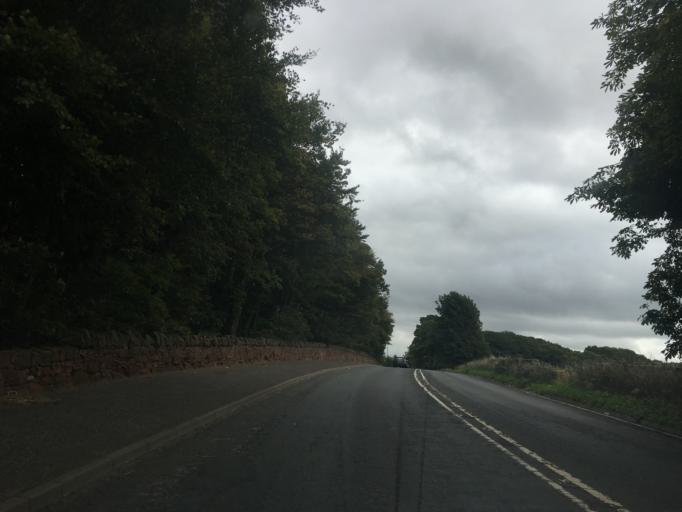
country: GB
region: Scotland
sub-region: Midlothian
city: Bonnyrigg
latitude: 55.8982
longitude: -3.1061
